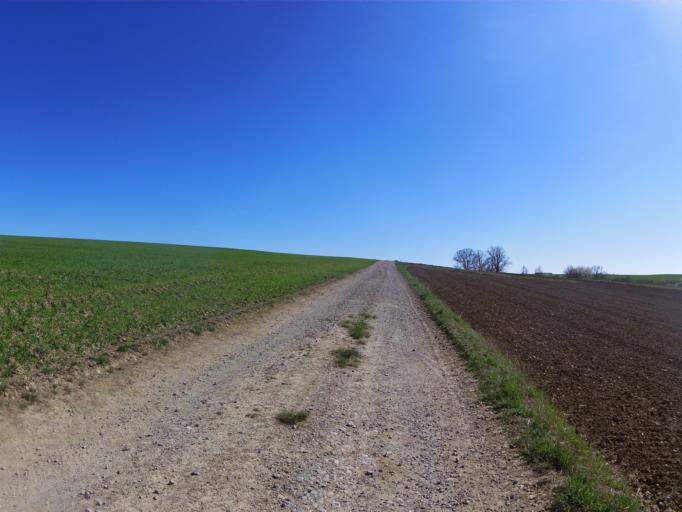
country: DE
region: Bavaria
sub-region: Regierungsbezirk Unterfranken
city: Biebelried
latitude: 49.8045
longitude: 10.0758
